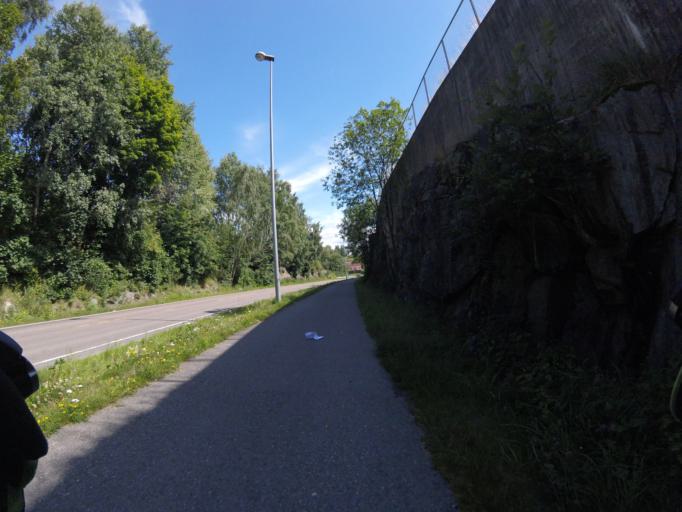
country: NO
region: Akershus
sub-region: Skedsmo
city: Lillestrom
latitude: 59.9524
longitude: 11.0203
